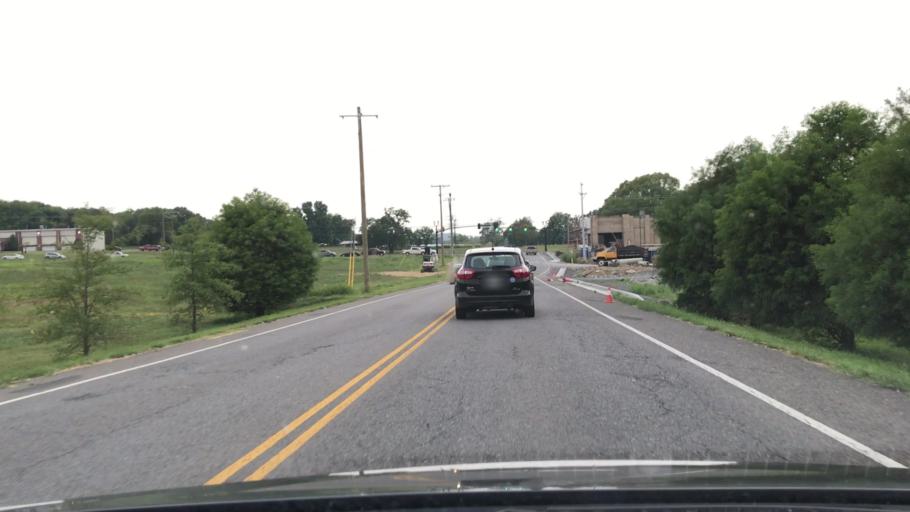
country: US
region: Tennessee
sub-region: Williamson County
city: Nolensville
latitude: 35.9503
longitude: -86.6657
